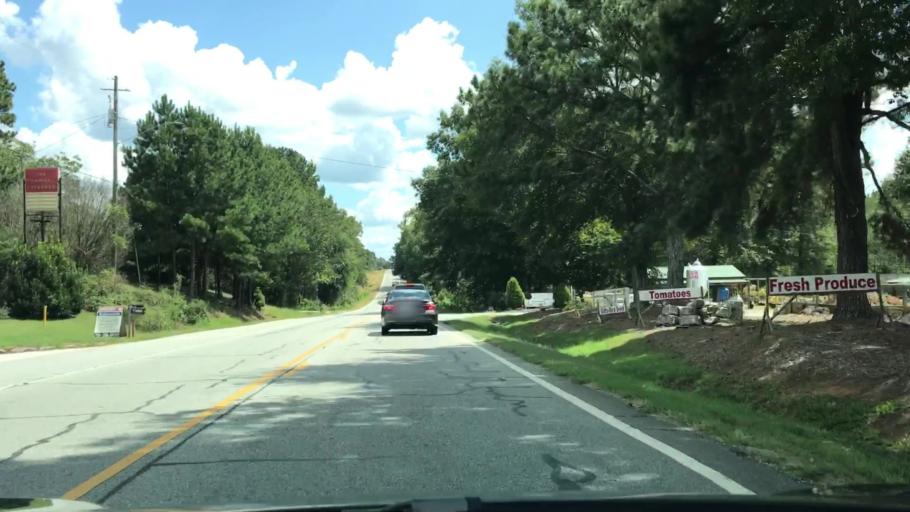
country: US
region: Georgia
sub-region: Oconee County
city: Watkinsville
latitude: 33.8513
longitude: -83.3969
